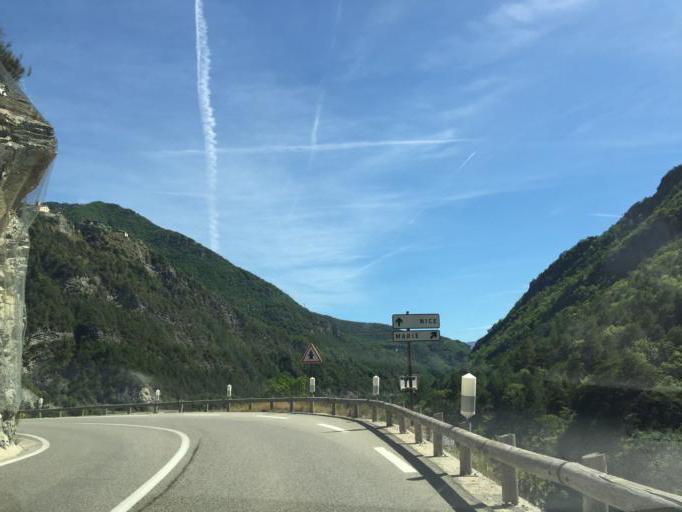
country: FR
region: Provence-Alpes-Cote d'Azur
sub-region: Departement des Alpes-Maritimes
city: Saint-Martin-Vesubie
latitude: 44.0366
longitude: 7.1280
